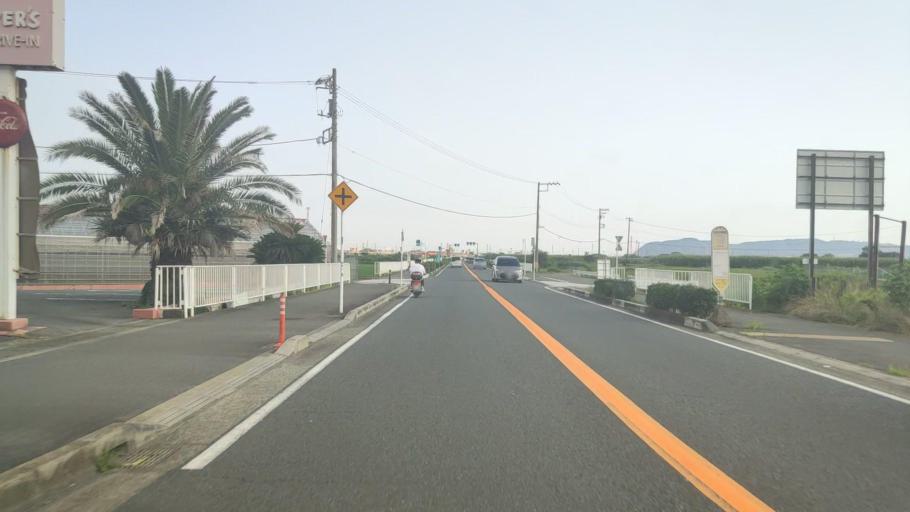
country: JP
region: Kanagawa
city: Isehara
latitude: 35.3701
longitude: 139.3217
